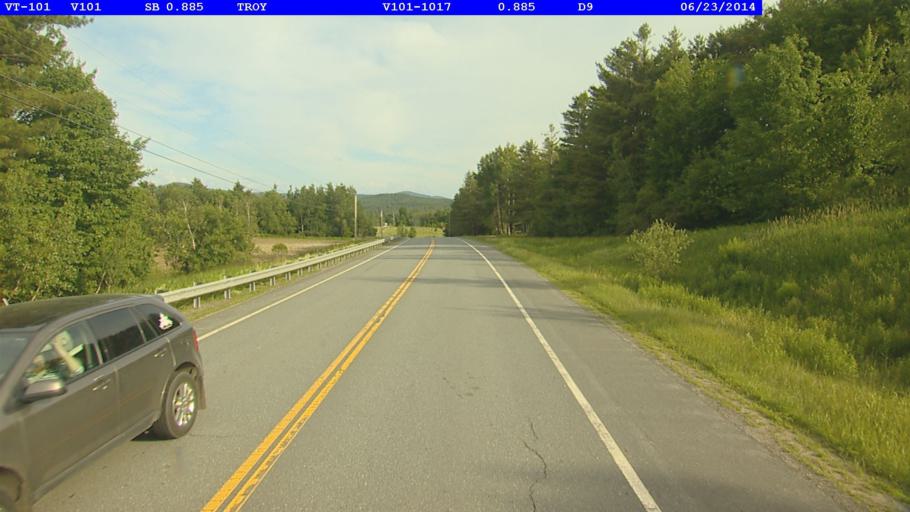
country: US
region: Vermont
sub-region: Orleans County
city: Newport
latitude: 44.9158
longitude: -72.4083
